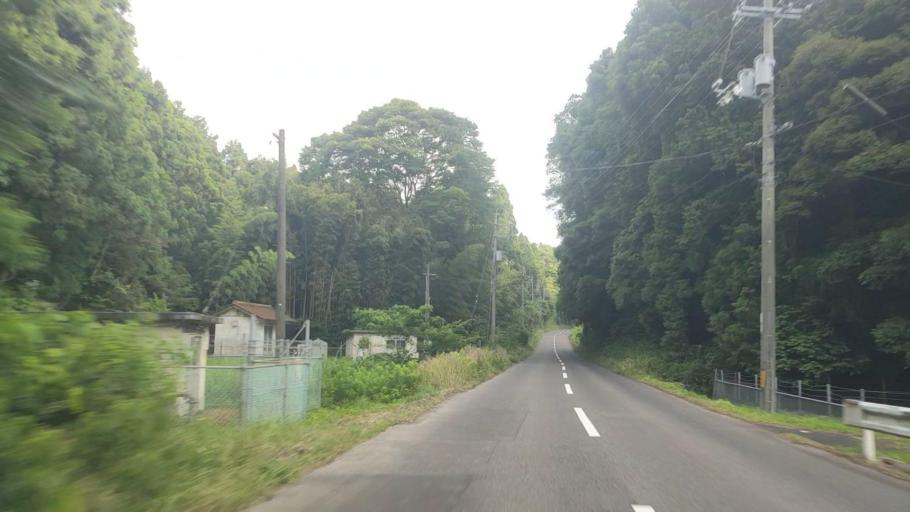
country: JP
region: Tottori
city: Kurayoshi
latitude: 35.4152
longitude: 133.7838
